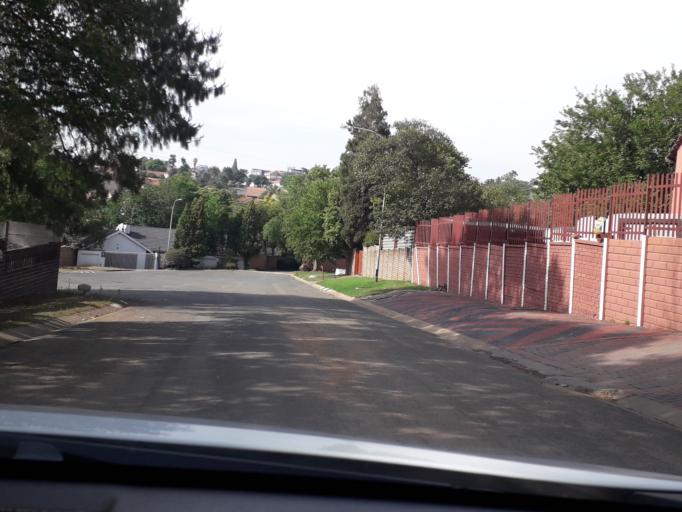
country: ZA
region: Gauteng
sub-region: City of Johannesburg Metropolitan Municipality
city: Modderfontein
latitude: -26.1201
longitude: 28.1091
